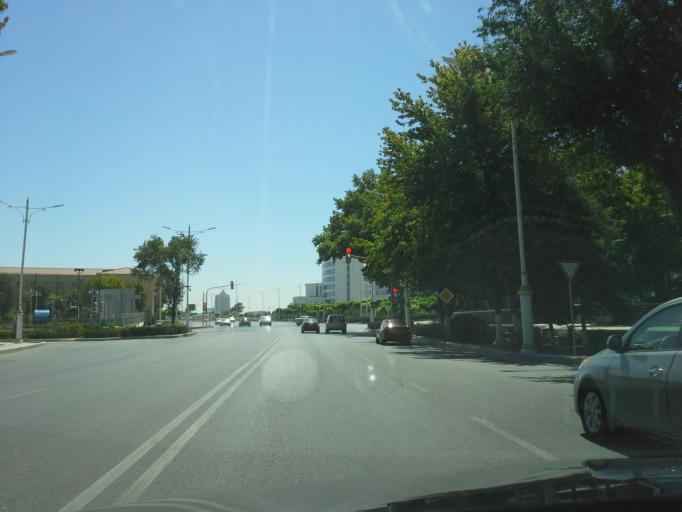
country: TM
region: Ahal
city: Ashgabat
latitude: 37.9436
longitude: 58.3593
